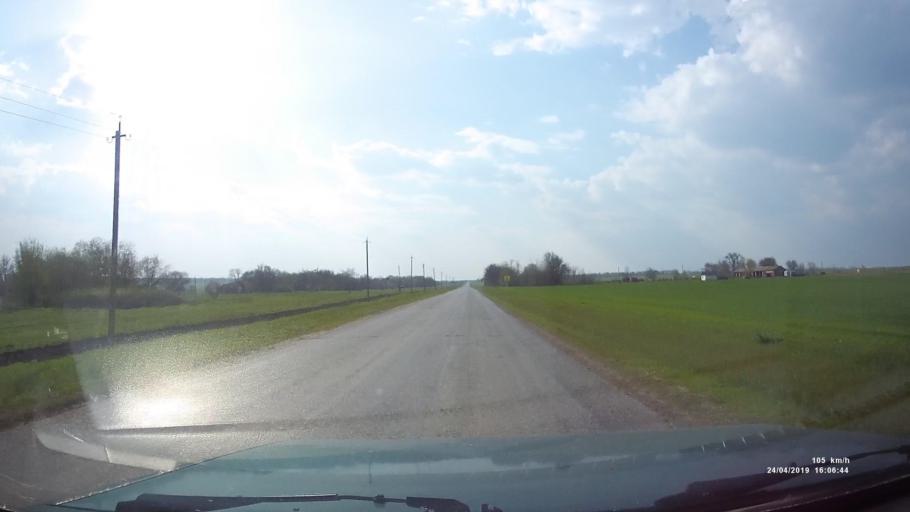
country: RU
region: Rostov
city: Sovetskoye
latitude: 46.6884
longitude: 42.3424
